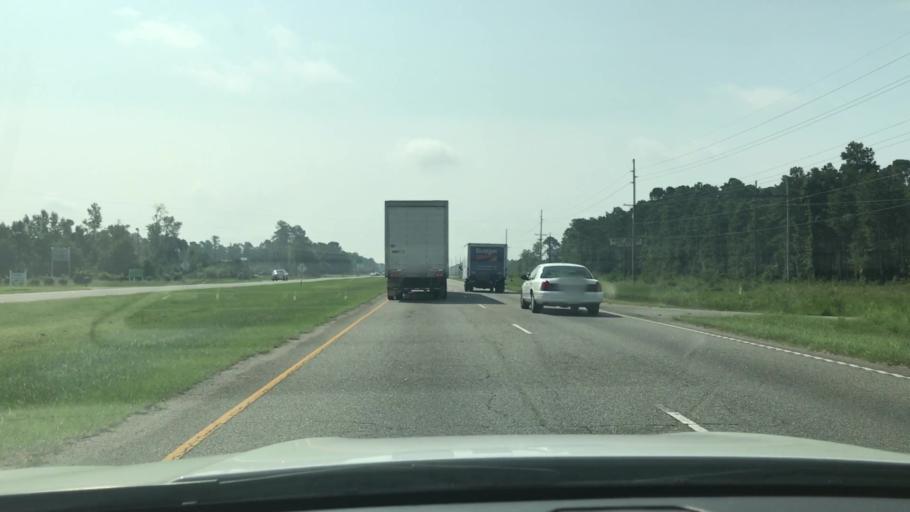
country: US
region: South Carolina
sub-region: Horry County
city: Red Hill
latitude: 33.7860
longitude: -78.9928
